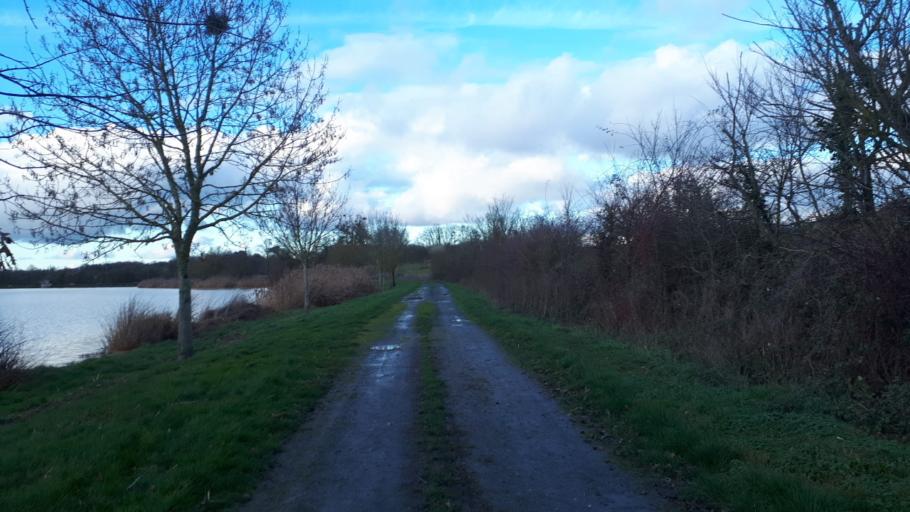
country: FR
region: Poitou-Charentes
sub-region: Departement de la Vienne
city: Pleumartin
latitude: 46.6344
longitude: 0.7659
